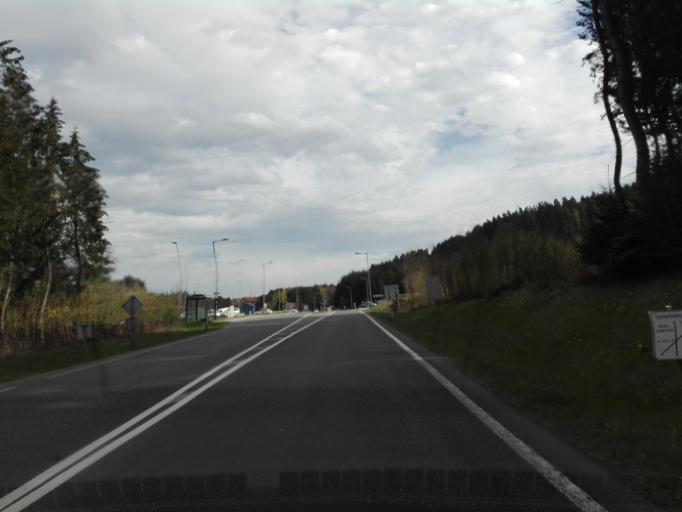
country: AT
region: Upper Austria
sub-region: Politischer Bezirk Rohrbach
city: Kleinzell im Muehlkreis
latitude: 48.4595
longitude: 14.0301
